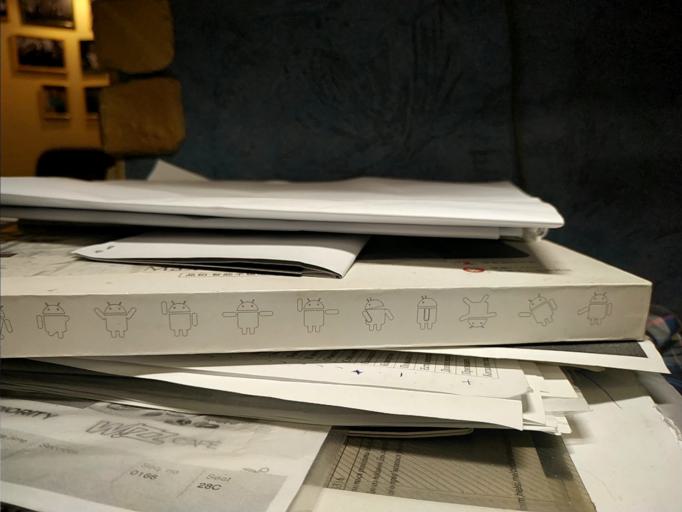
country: RU
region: Tverskaya
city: Zubtsov
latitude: 56.0848
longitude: 34.7762
